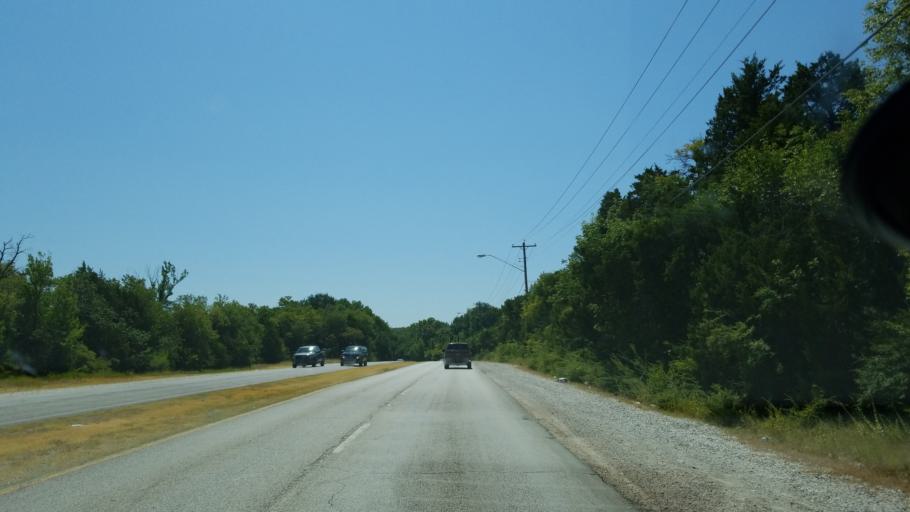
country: US
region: Texas
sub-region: Dallas County
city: Cockrell Hill
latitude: 32.7394
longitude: -96.9001
